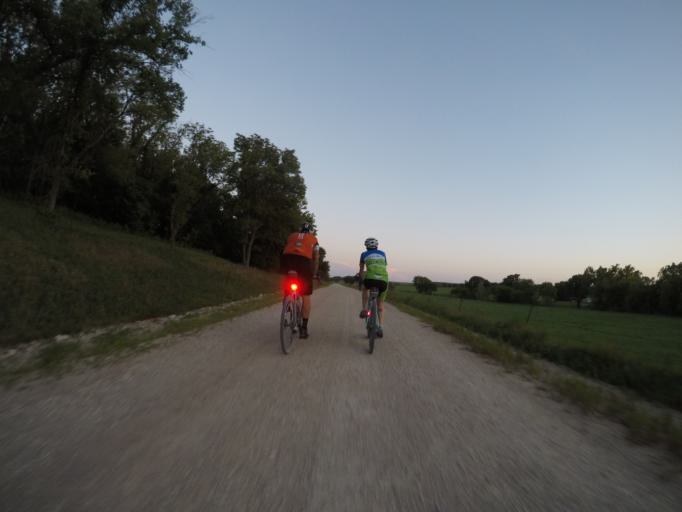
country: US
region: Kansas
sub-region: Riley County
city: Ogden
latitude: 38.9772
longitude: -96.5634
